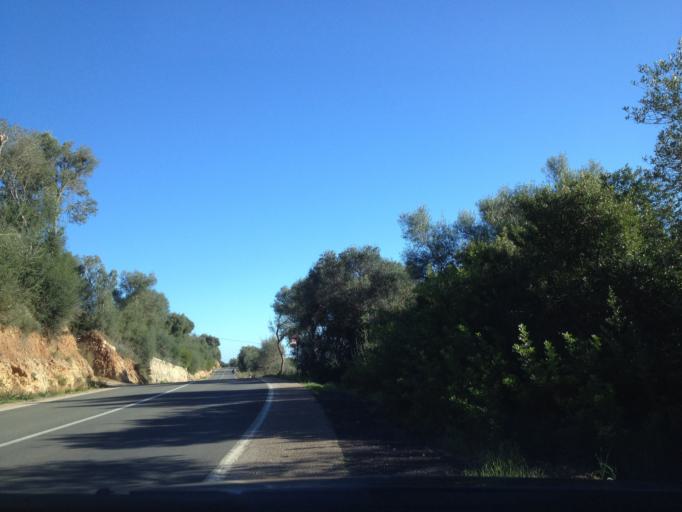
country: ES
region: Balearic Islands
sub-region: Illes Balears
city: Sineu
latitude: 39.6517
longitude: 3.0282
